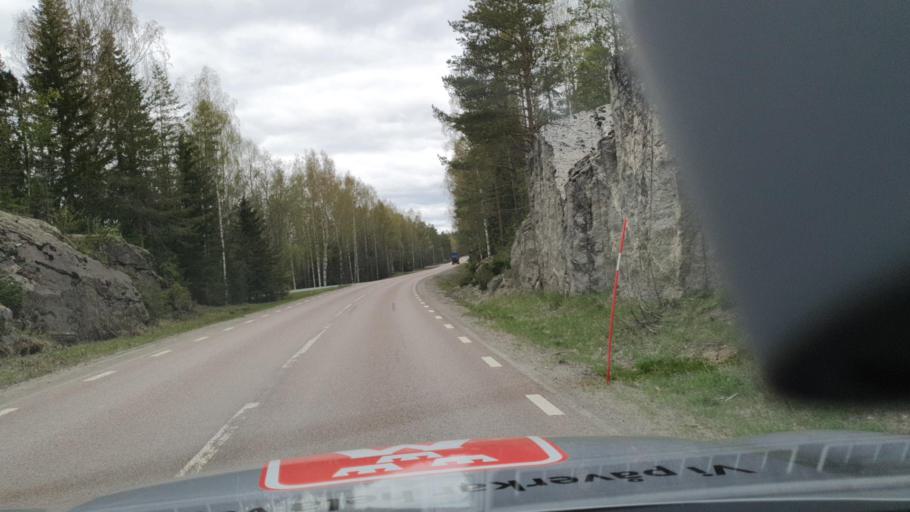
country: SE
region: Vaesternorrland
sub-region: OErnskoeldsviks Kommun
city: Husum
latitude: 63.3494
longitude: 19.1180
